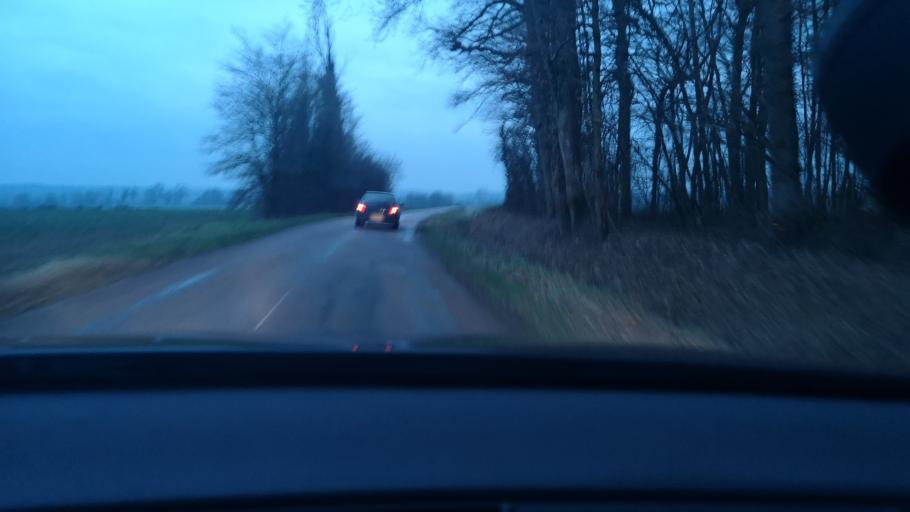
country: FR
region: Bourgogne
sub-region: Departement de Saone-et-Loire
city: Gergy
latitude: 46.9639
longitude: 4.9297
